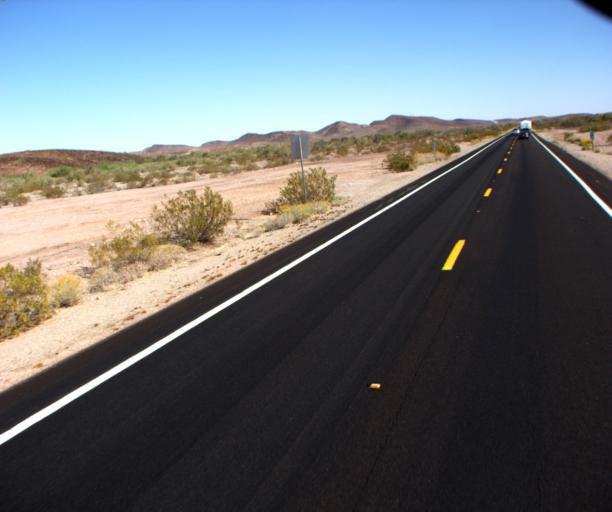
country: US
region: Arizona
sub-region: La Paz County
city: Quartzsite
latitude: 33.2034
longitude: -114.2671
